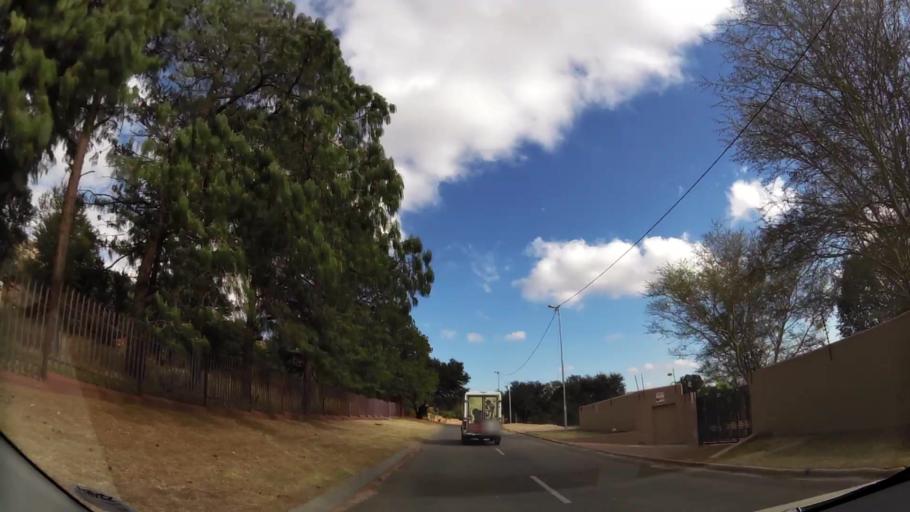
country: ZA
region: Gauteng
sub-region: West Rand District Municipality
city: Muldersdriseloop
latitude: -26.0929
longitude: 27.8531
